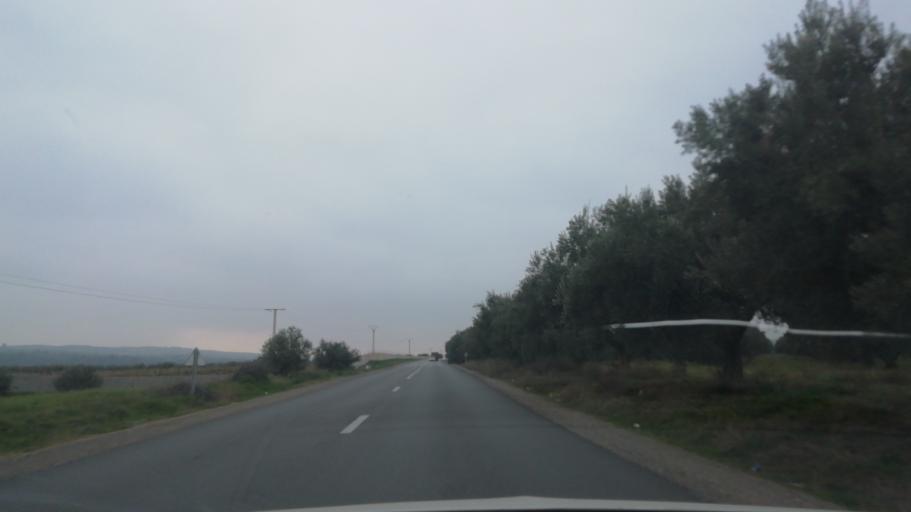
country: DZ
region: Sidi Bel Abbes
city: Sfizef
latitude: 35.2683
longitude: -0.1616
